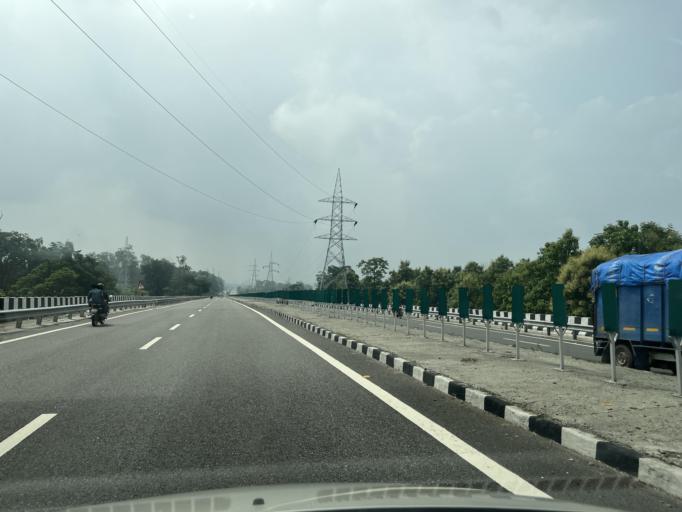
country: IN
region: Uttarakhand
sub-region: Dehradun
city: Raiwala
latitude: 30.0974
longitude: 78.1801
